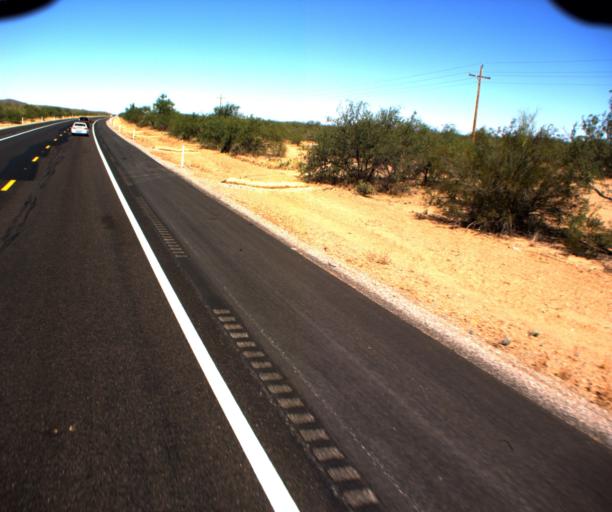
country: US
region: Arizona
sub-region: Pima County
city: Sells
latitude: 31.9201
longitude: -111.8274
